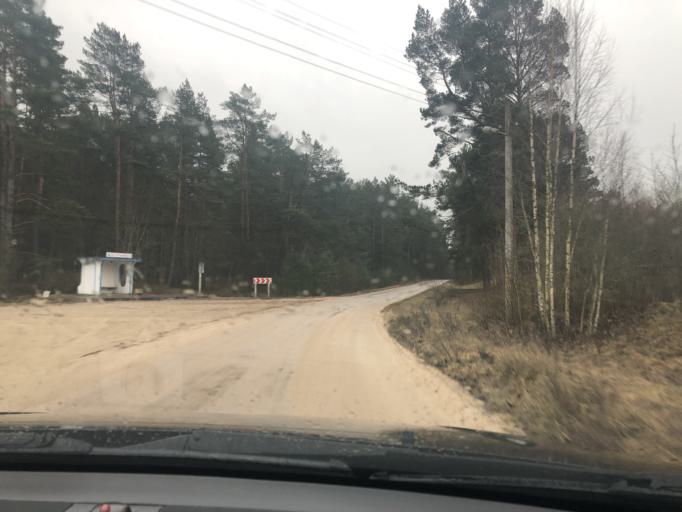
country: BY
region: Grodnenskaya
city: Skidal'
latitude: 53.8568
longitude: 24.2518
